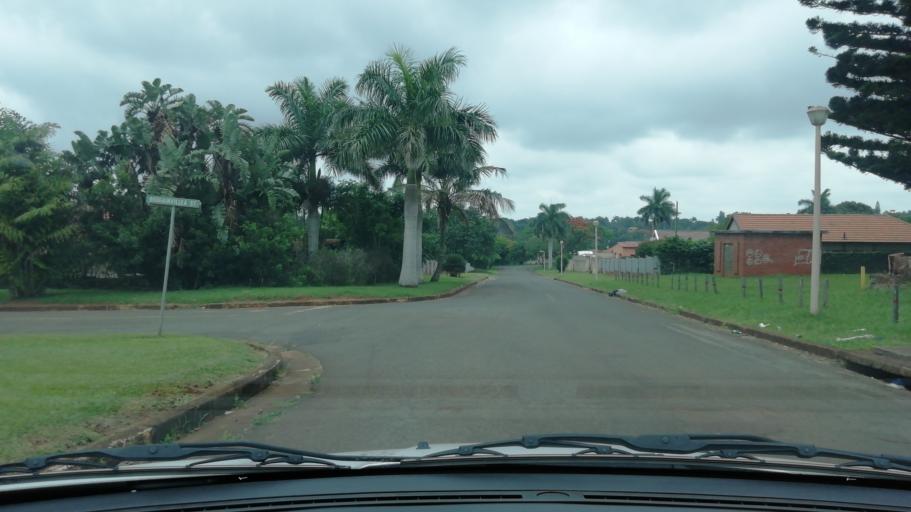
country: ZA
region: KwaZulu-Natal
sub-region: uThungulu District Municipality
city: Empangeni
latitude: -28.7611
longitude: 31.9027
